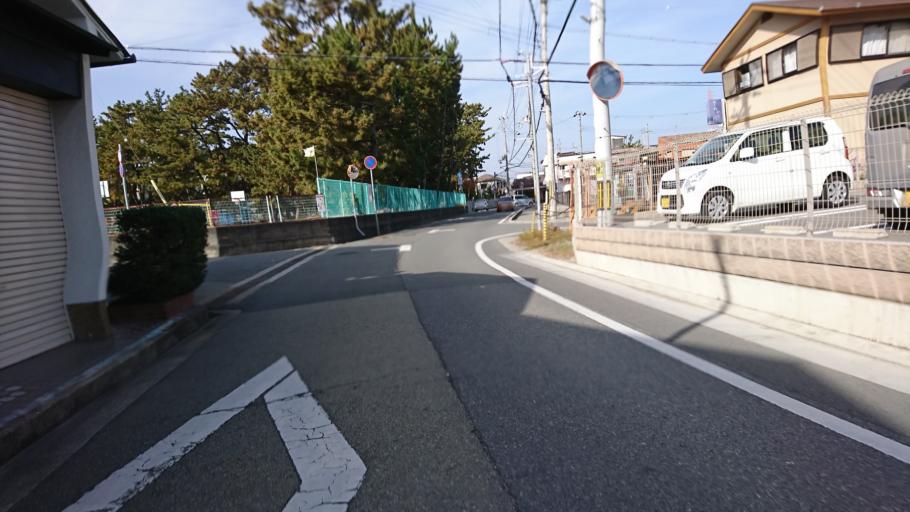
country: JP
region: Hyogo
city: Kakogawacho-honmachi
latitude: 34.7380
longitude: 134.8359
